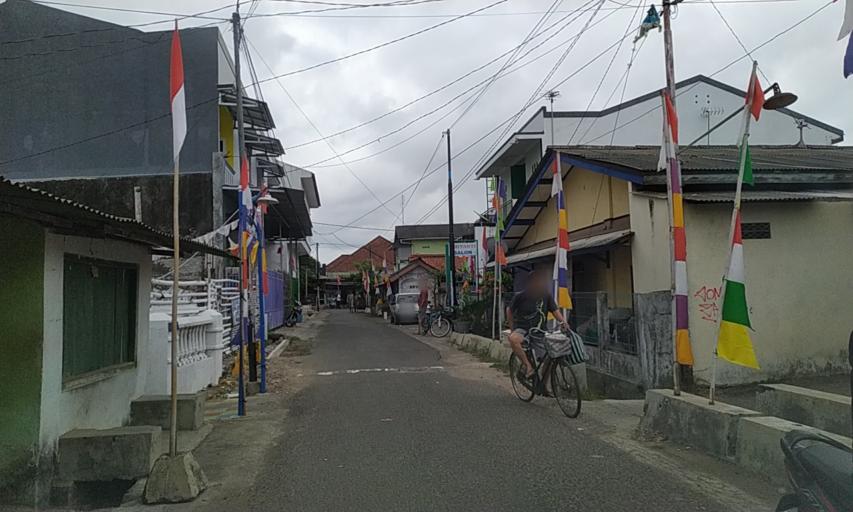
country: ID
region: Central Java
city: Karangbadar Kidul
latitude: -7.7352
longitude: 109.0083
